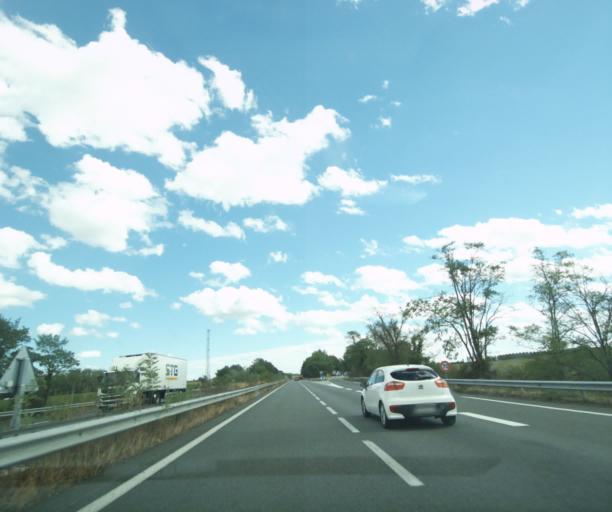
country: FR
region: Aquitaine
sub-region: Departement du Lot-et-Garonne
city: Meilhan-sur-Garonne
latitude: 44.4760
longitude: 0.0333
